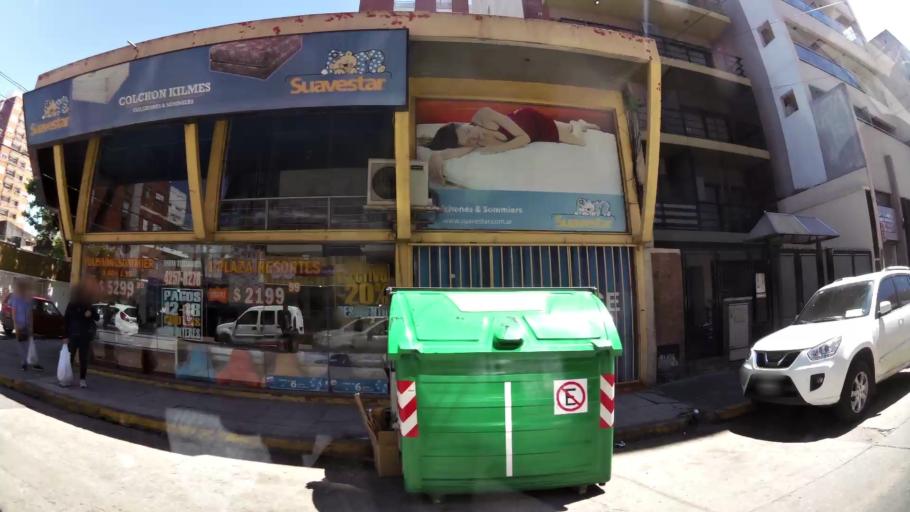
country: AR
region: Buenos Aires
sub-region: Partido de Quilmes
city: Quilmes
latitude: -34.7251
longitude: -58.2573
